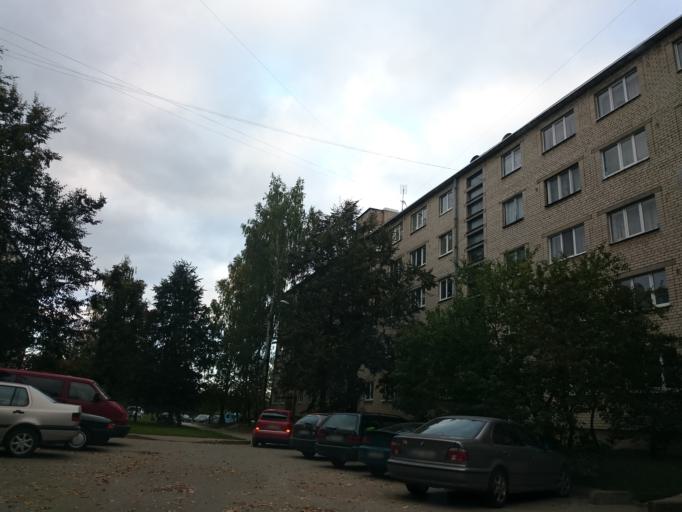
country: LV
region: Adazi
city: Adazi
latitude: 57.0796
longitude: 24.3283
